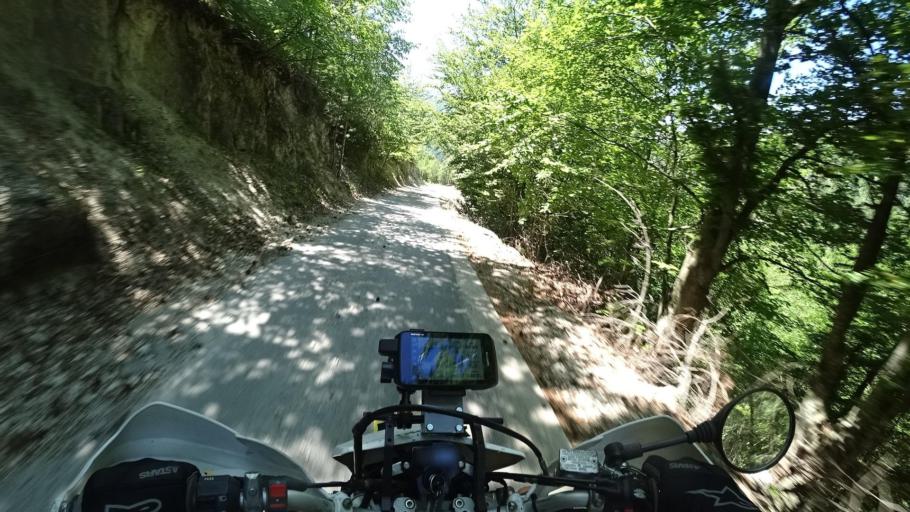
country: BA
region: Federation of Bosnia and Herzegovina
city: Polje-Bijela
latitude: 43.6288
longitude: 18.0279
